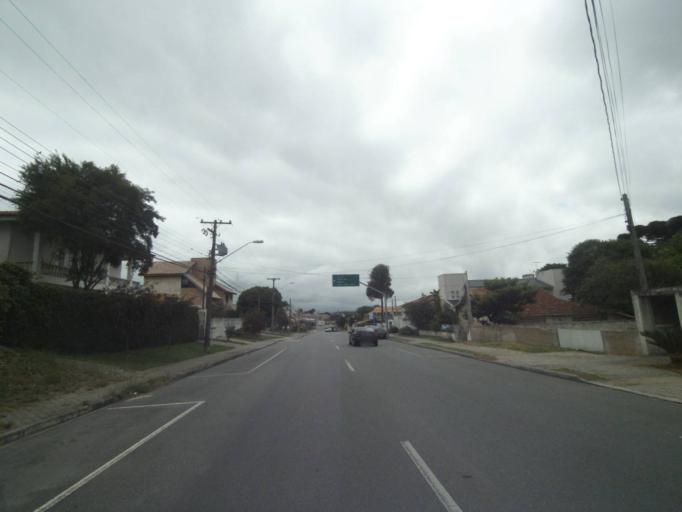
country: BR
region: Parana
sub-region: Pinhais
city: Pinhais
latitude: -25.4367
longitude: -49.2301
